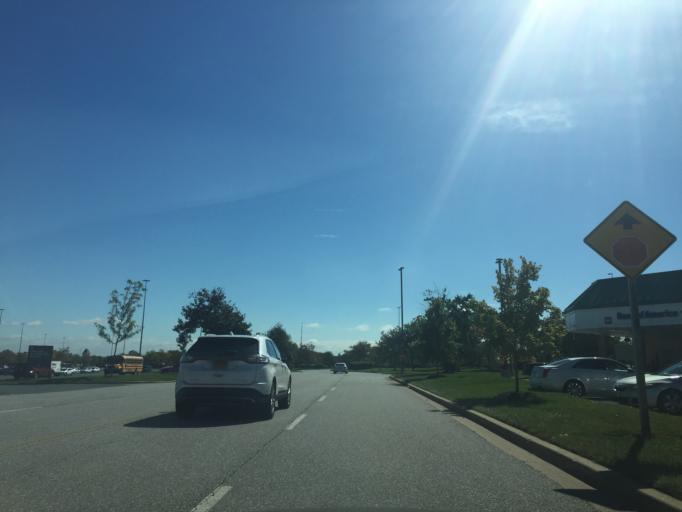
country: US
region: Maryland
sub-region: Baltimore County
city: Rossville
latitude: 39.3740
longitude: -76.4709
